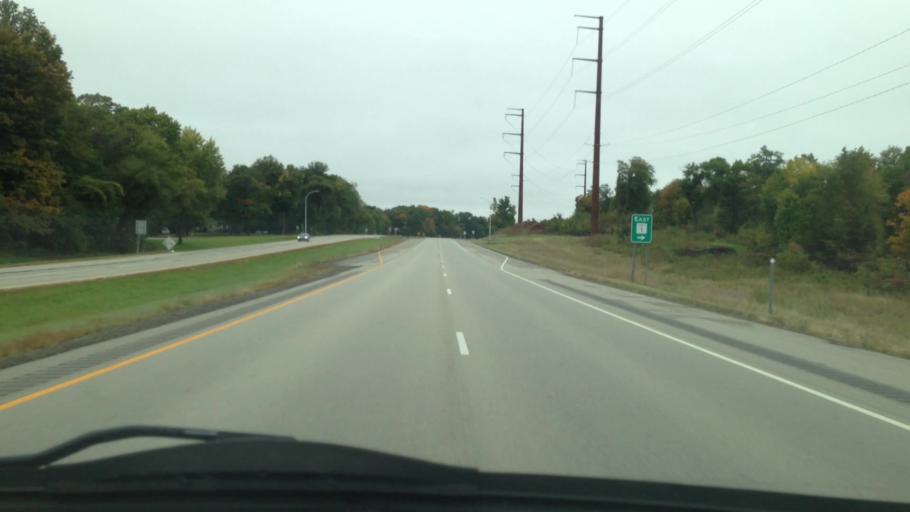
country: US
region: Minnesota
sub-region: Goodhue County
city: Cannon Falls
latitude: 44.4187
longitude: -92.8710
